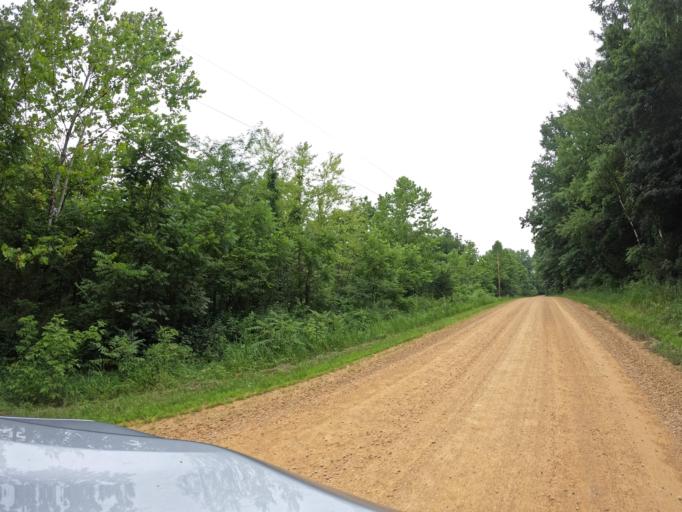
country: US
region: Illinois
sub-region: Carroll County
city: Savanna
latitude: 41.9974
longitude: -90.1762
